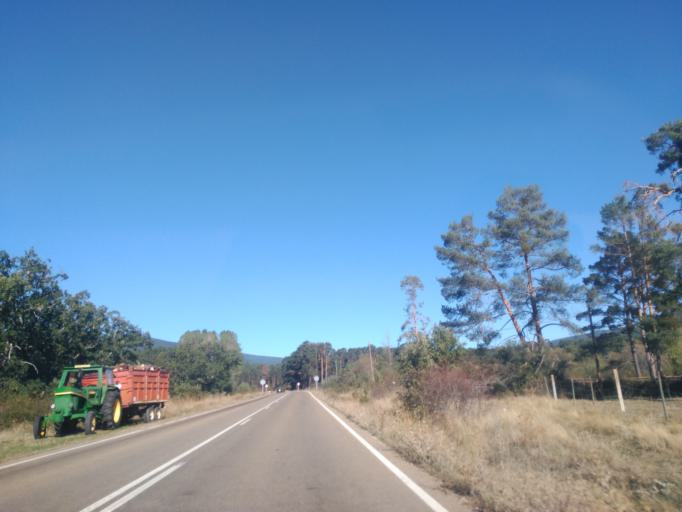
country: ES
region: Castille and Leon
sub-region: Provincia de Soria
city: Vinuesa
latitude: 41.9215
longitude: -2.7607
